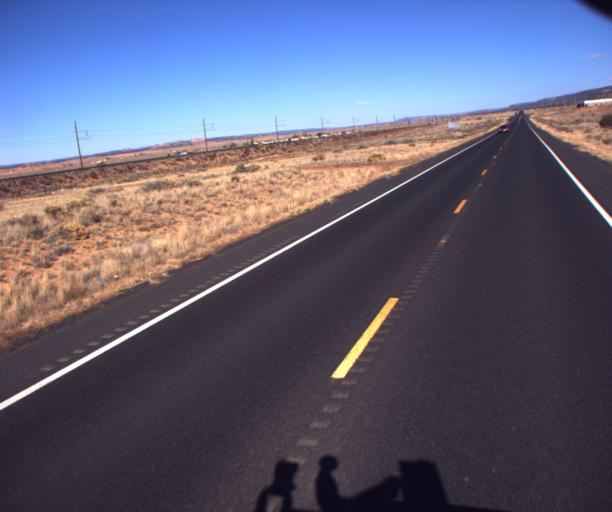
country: US
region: Arizona
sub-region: Coconino County
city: Kaibito
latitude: 36.4581
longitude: -110.6995
